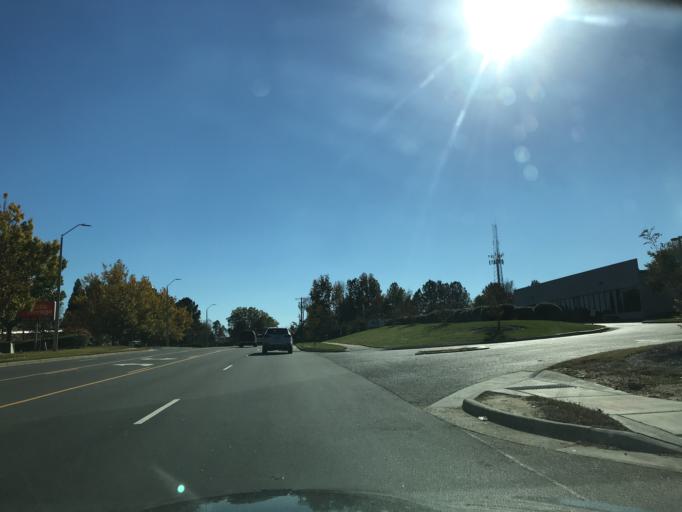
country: US
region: North Carolina
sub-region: Wake County
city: Raleigh
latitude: 35.8430
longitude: -78.6014
